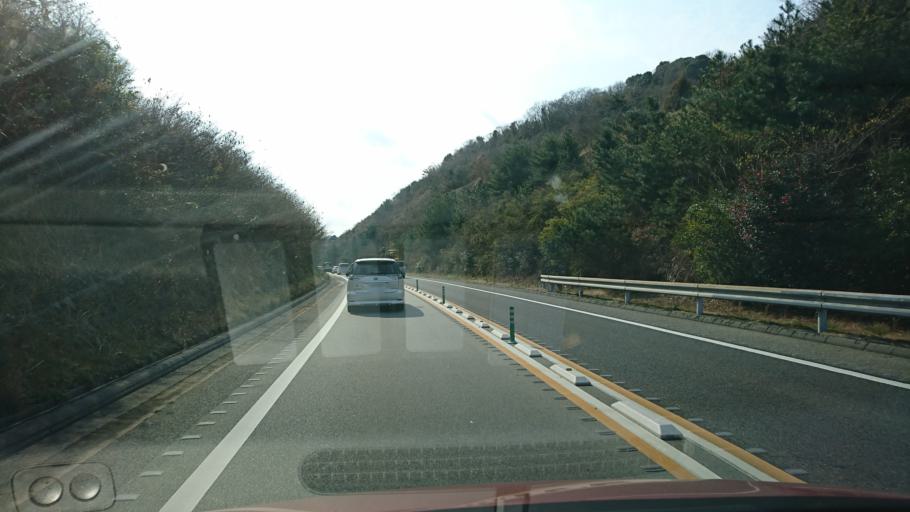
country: JP
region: Hiroshima
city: Innoshima
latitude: 34.3450
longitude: 133.1618
